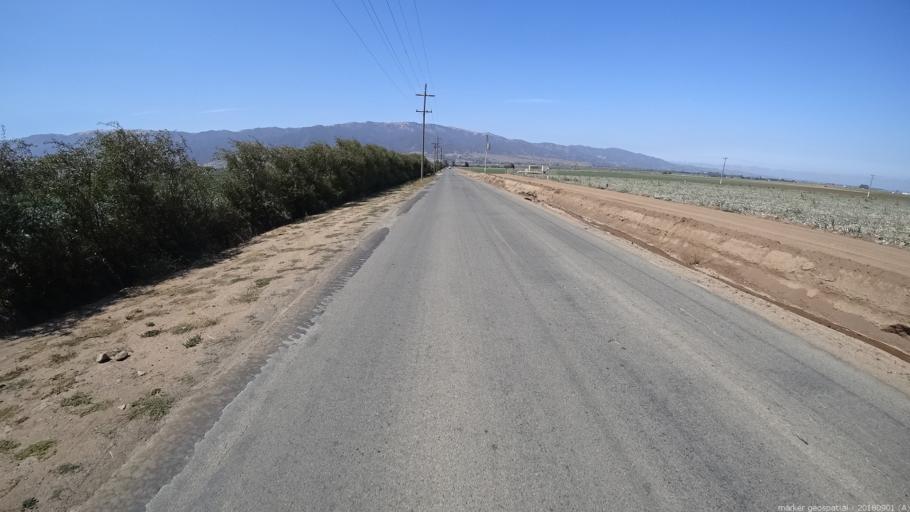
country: US
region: California
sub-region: Monterey County
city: Chualar
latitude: 36.5756
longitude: -121.5127
